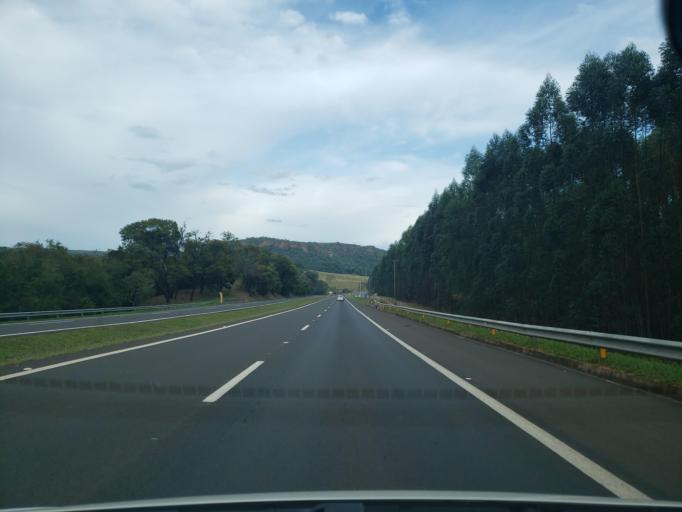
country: BR
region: Sao Paulo
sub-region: Itirapina
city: Itirapina
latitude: -22.2711
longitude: -47.9403
